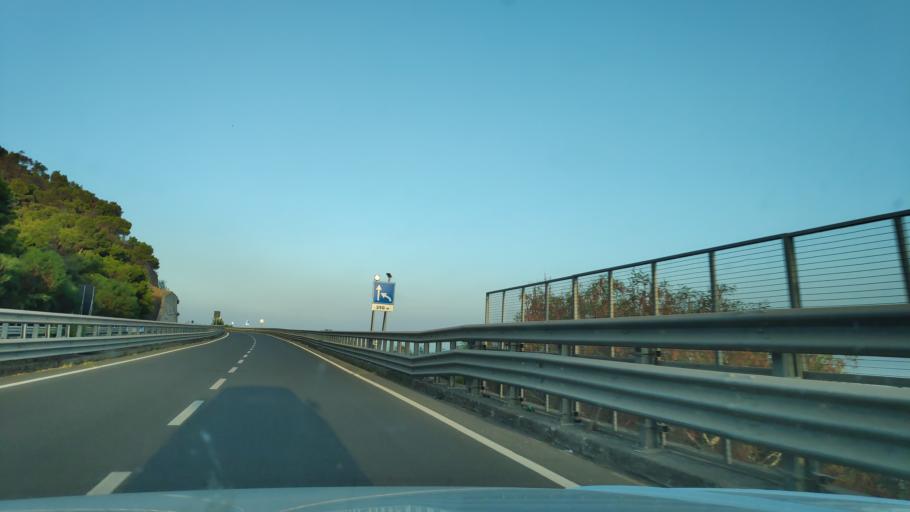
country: IT
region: Calabria
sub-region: Provincia di Reggio Calabria
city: Palizzi Marina
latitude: 37.9203
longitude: 15.9619
